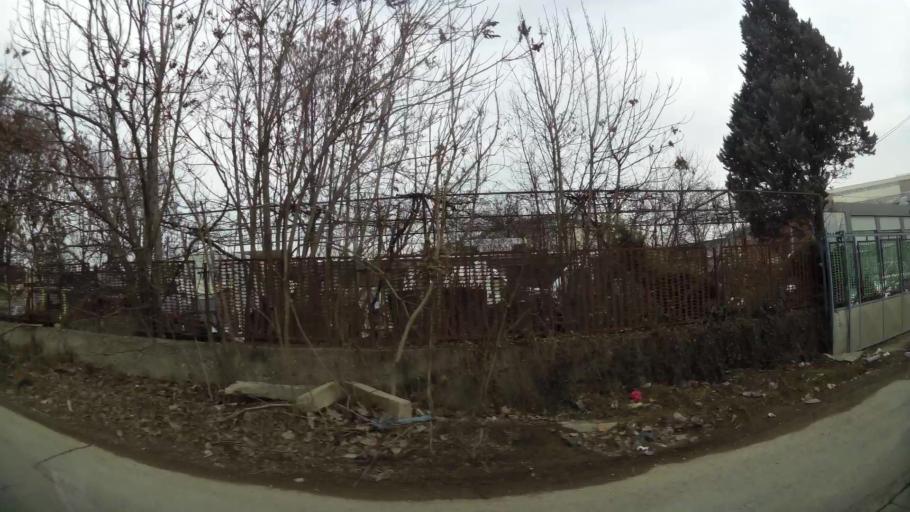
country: MK
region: Suto Orizari
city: Suto Orizare
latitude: 42.0314
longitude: 21.4048
